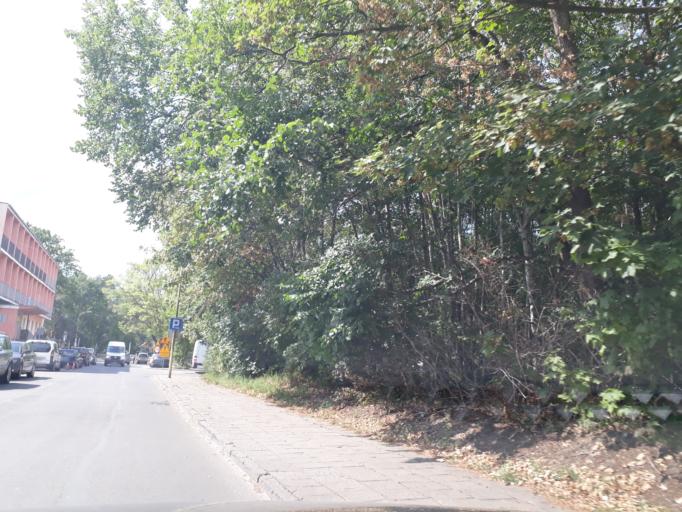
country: PL
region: West Pomeranian Voivodeship
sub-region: Swinoujscie
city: Swinoujscie
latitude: 53.9209
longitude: 14.2235
